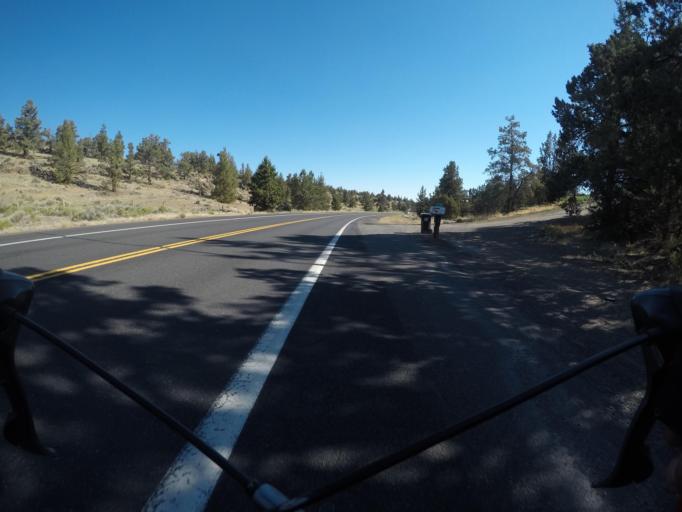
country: US
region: Oregon
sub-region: Deschutes County
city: Redmond
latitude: 44.2501
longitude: -121.2760
